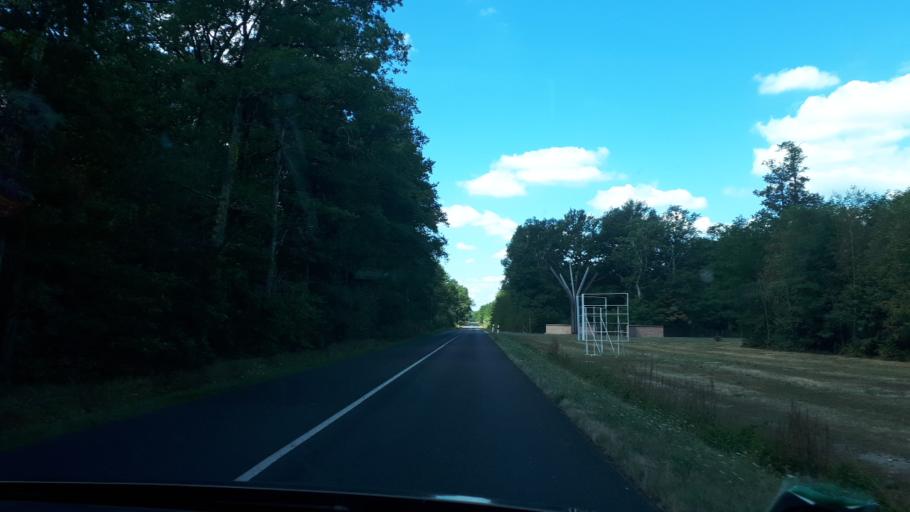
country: FR
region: Centre
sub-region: Departement du Loir-et-Cher
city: Neung-sur-Beuvron
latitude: 47.5345
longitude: 1.7641
